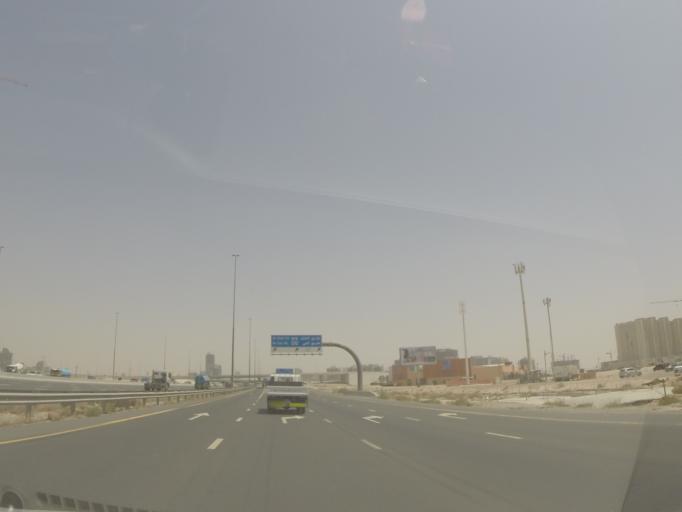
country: AE
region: Dubai
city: Dubai
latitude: 25.0430
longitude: 55.1991
